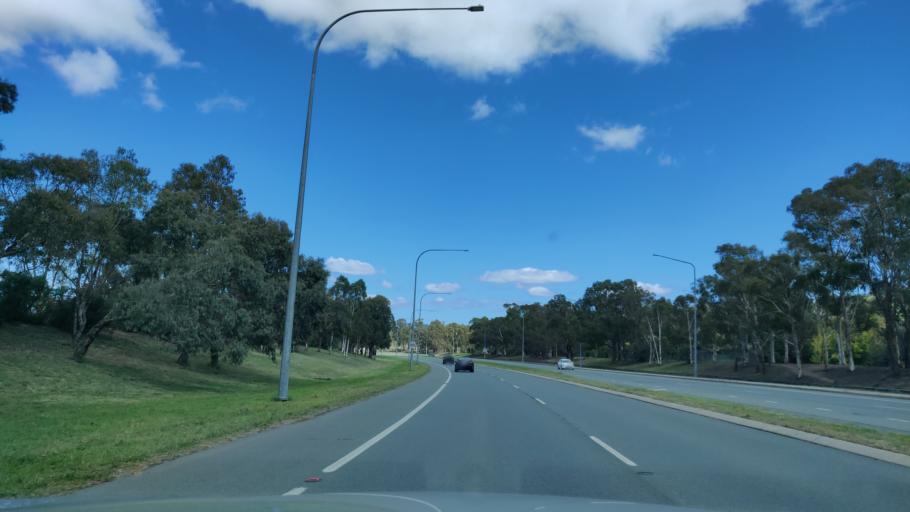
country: AU
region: Australian Capital Territory
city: Macarthur
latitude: -35.3995
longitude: 149.0668
